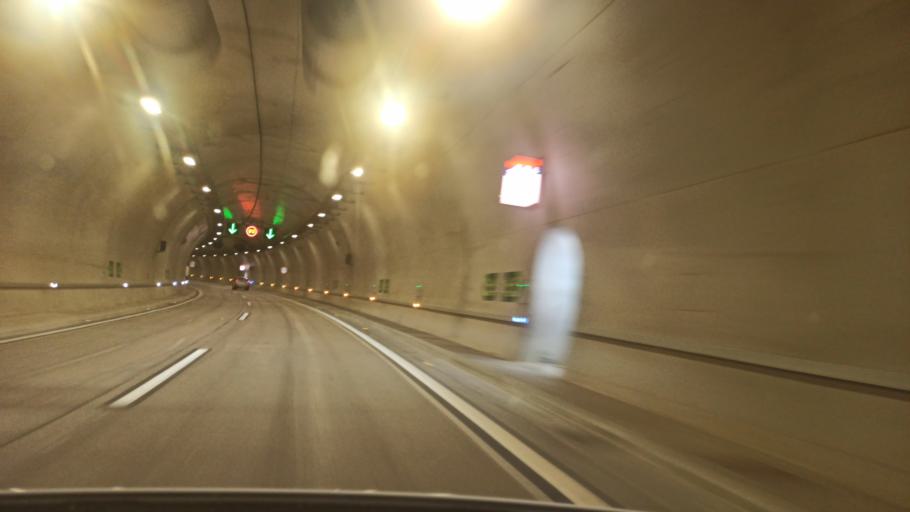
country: ES
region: Catalonia
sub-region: Provincia de Barcelona
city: Vallirana
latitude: 41.3801
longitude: 1.9296
